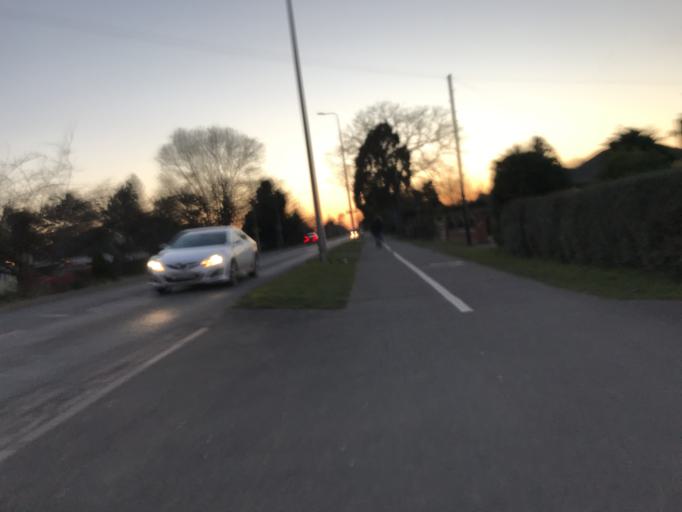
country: GB
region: England
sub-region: Lincolnshire
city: Holton le Clay
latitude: 53.5230
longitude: -0.0679
